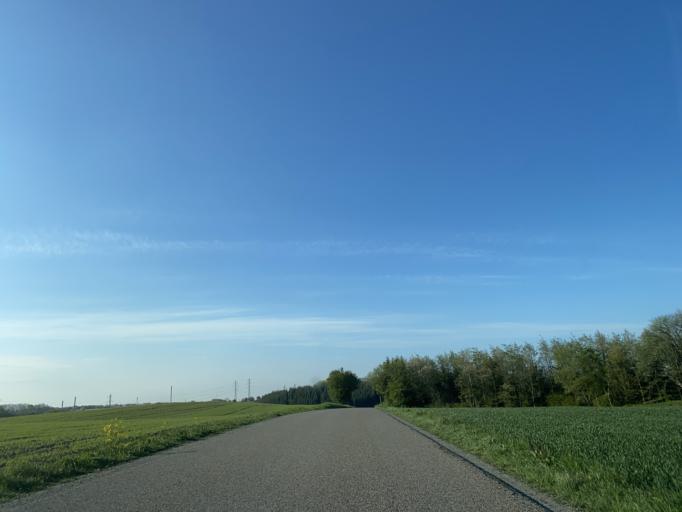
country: DK
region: Central Jutland
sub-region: Silkeborg Kommune
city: Silkeborg
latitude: 56.2138
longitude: 9.5618
